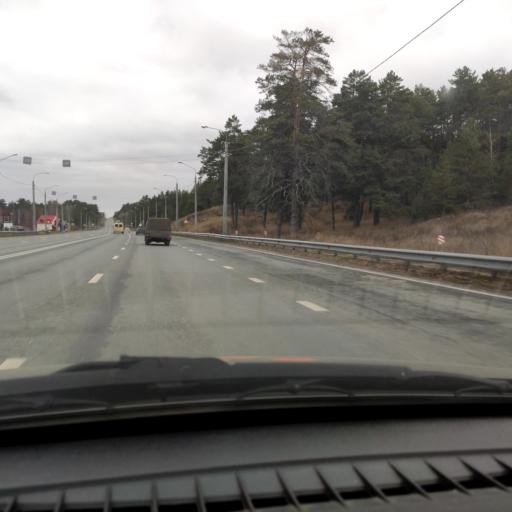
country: RU
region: Samara
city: Volzhskiy
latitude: 53.4368
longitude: 50.1120
